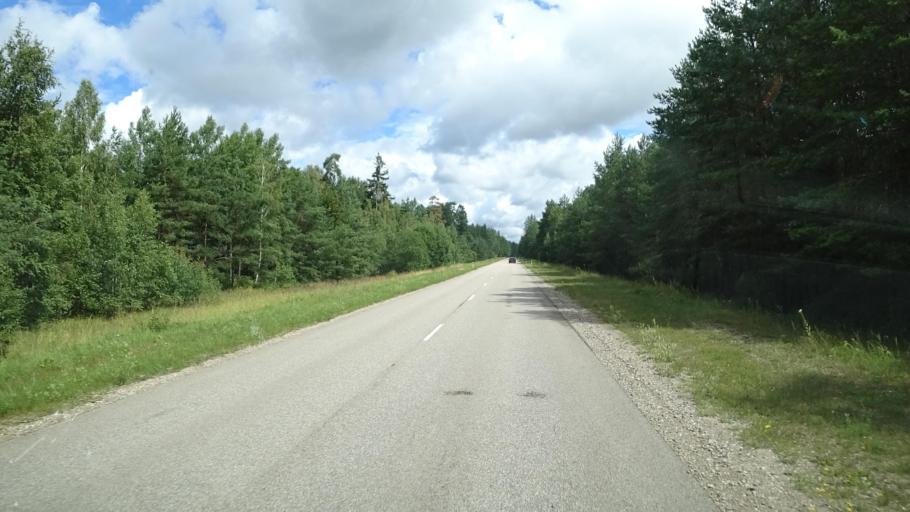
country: LV
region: Pavilostas
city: Pavilosta
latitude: 56.7212
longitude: 21.1888
